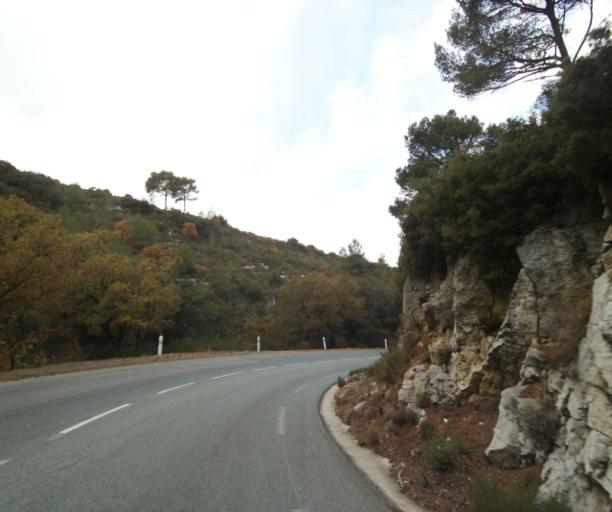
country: FR
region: Provence-Alpes-Cote d'Azur
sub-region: Departement des Bouches-du-Rhone
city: Cuges-les-Pins
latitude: 43.2657
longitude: 5.6622
